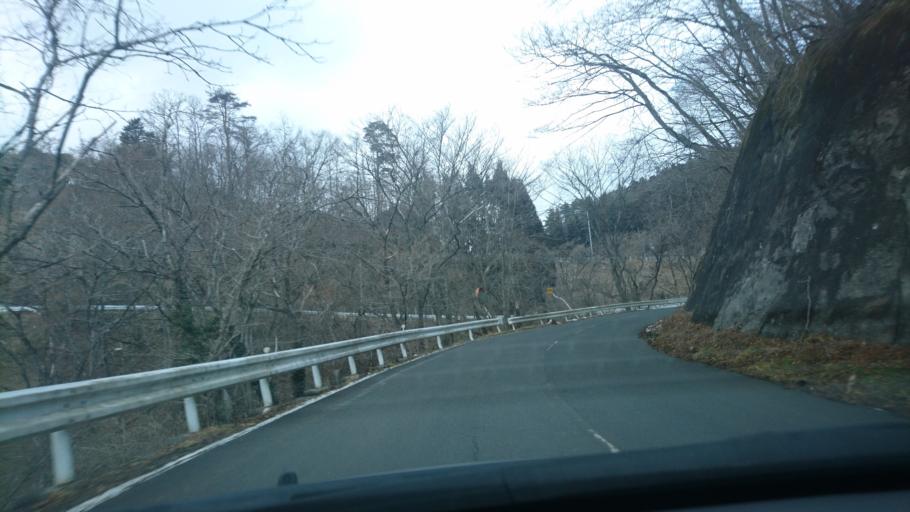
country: JP
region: Iwate
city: Ofunato
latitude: 38.9130
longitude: 141.5123
